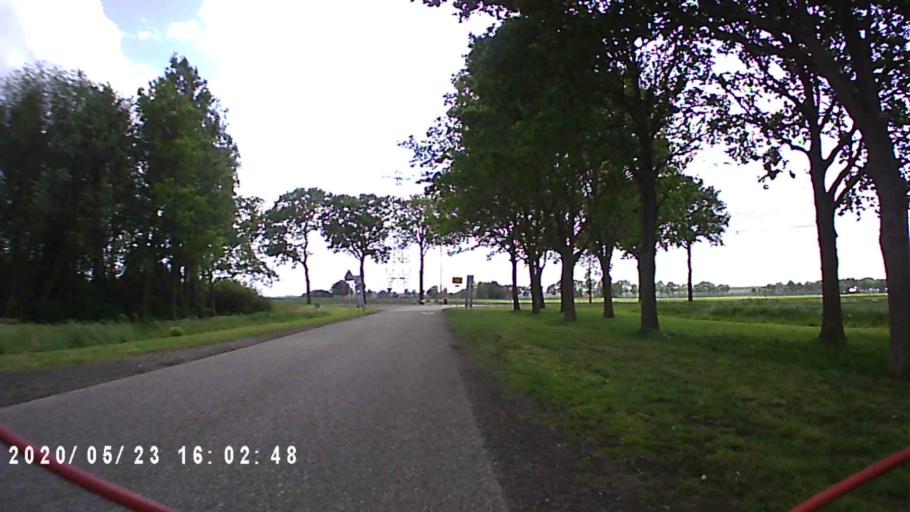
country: NL
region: Groningen
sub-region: Gemeente Delfzijl
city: Delfzijl
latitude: 53.2451
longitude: 6.8995
